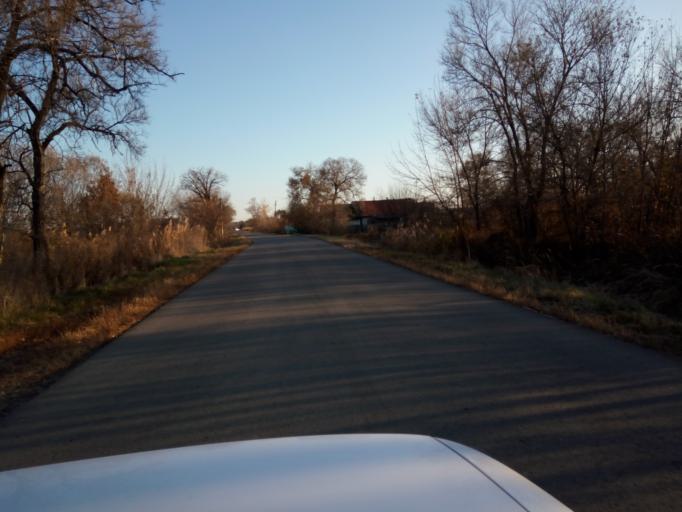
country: RU
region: Primorskiy
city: Lazo
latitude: 45.8619
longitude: 133.6408
